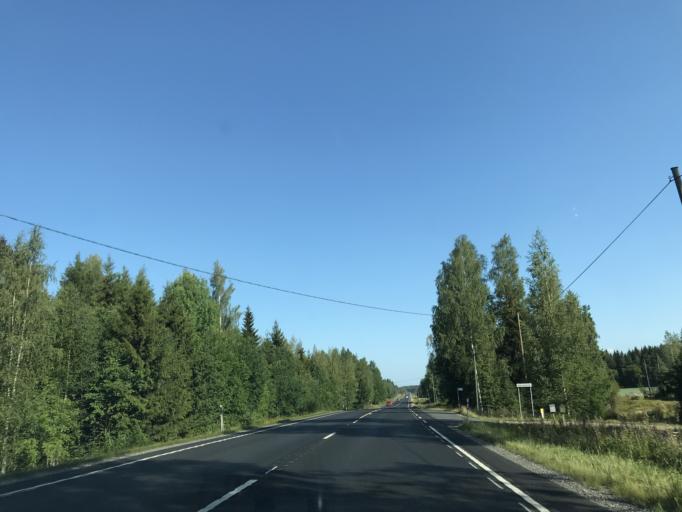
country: FI
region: Paijanne Tavastia
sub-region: Lahti
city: Lahti
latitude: 61.0796
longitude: 25.6590
